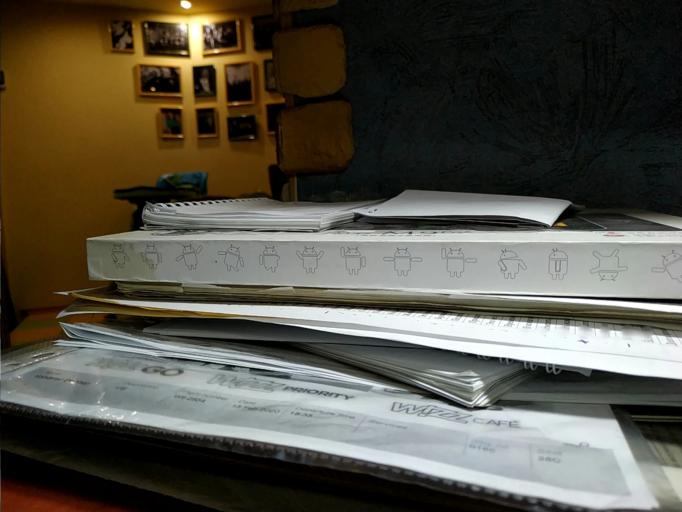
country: RU
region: Arkhangelskaya
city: Konevo
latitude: 62.1203
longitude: 38.9581
